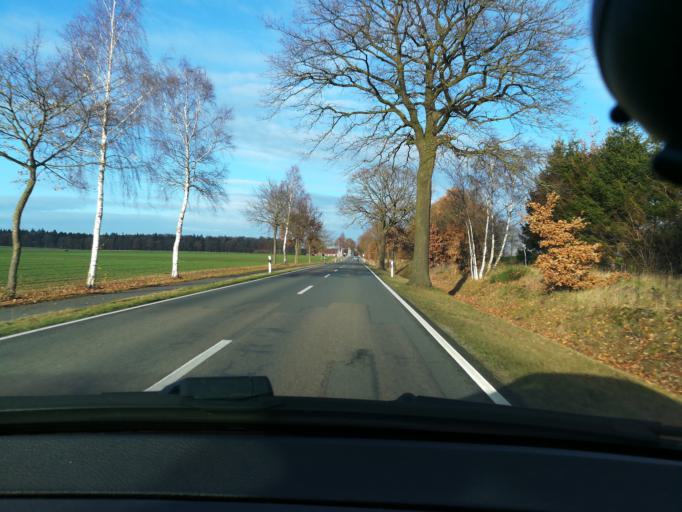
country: DE
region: Lower Saxony
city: Schwaforden
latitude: 52.7175
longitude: 8.8144
